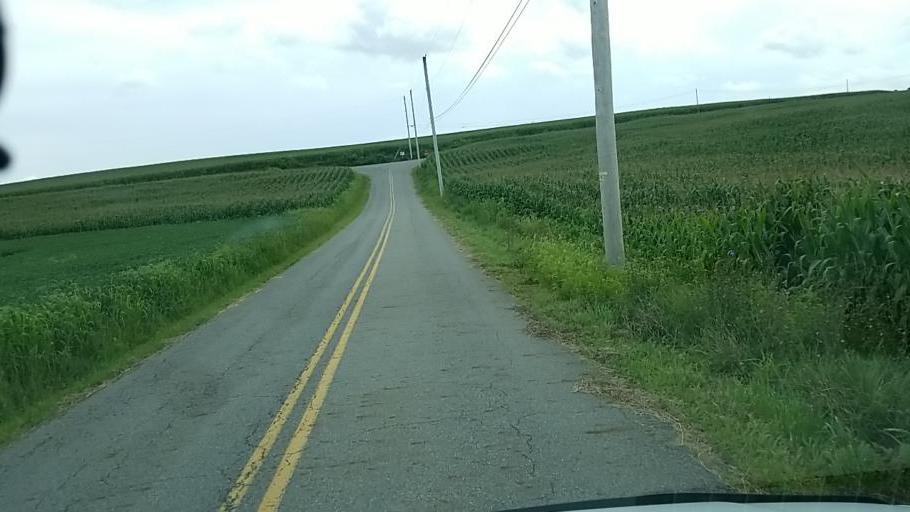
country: US
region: Pennsylvania
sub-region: Dauphin County
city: Elizabethville
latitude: 40.6499
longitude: -76.8350
